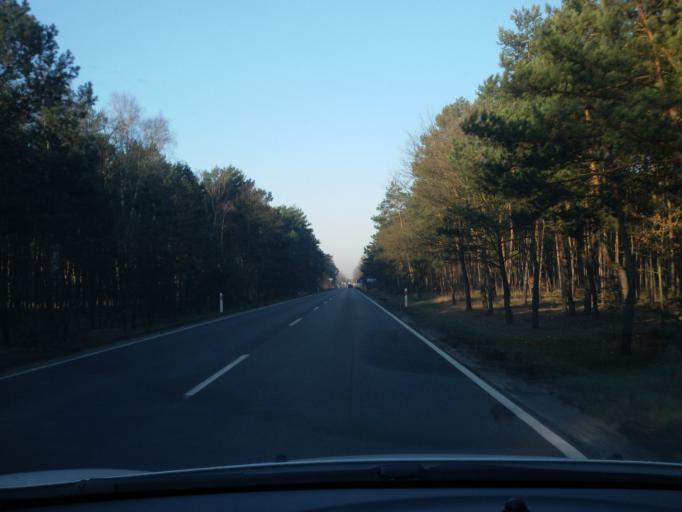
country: PL
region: Lubusz
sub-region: Powiat wschowski
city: Wschowa
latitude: 51.8197
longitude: 16.3984
